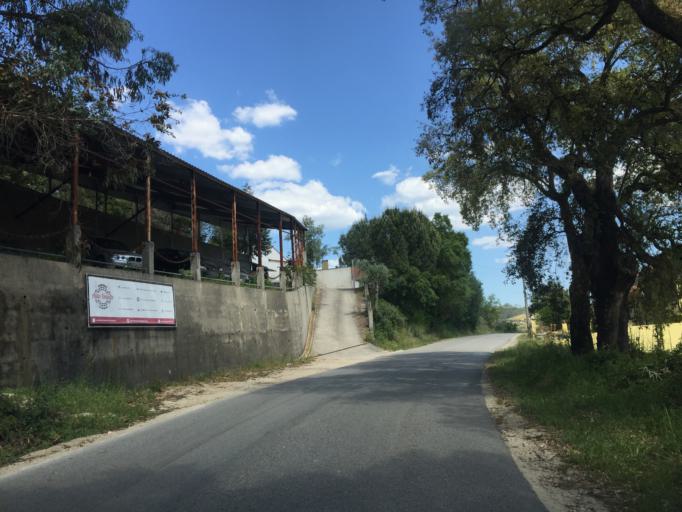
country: PT
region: Leiria
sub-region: Alvaiazere
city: Alvaiazere
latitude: 39.7585
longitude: -8.4645
